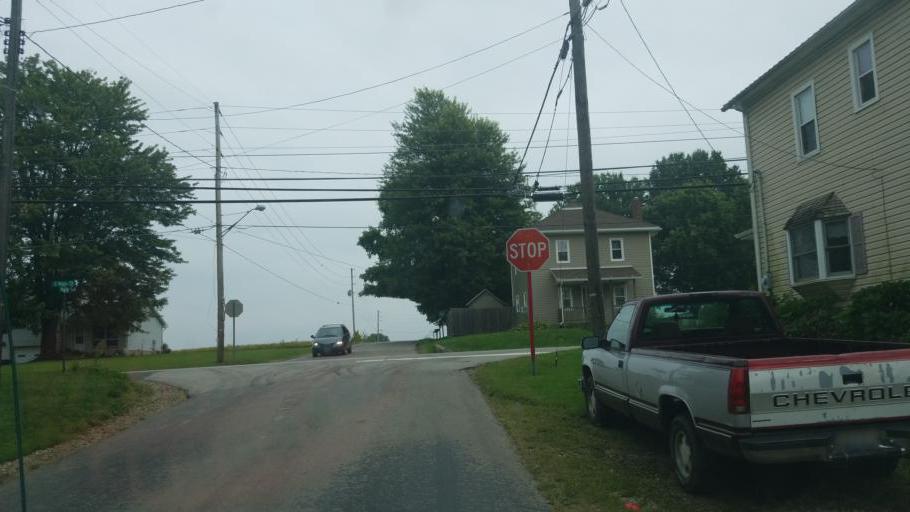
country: US
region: Ohio
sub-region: Wayne County
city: Creston
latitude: 40.9601
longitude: -81.8994
